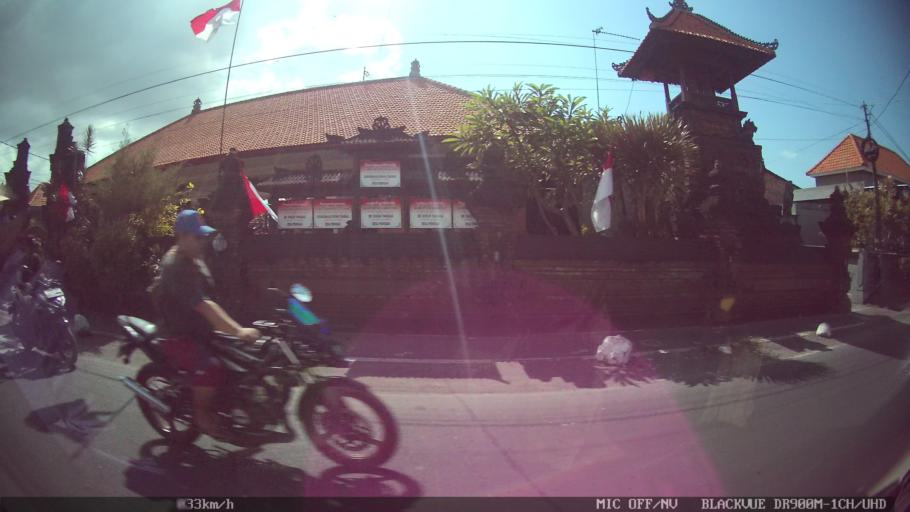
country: ID
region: Bali
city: Karyadharma
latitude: -8.7022
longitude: 115.1975
